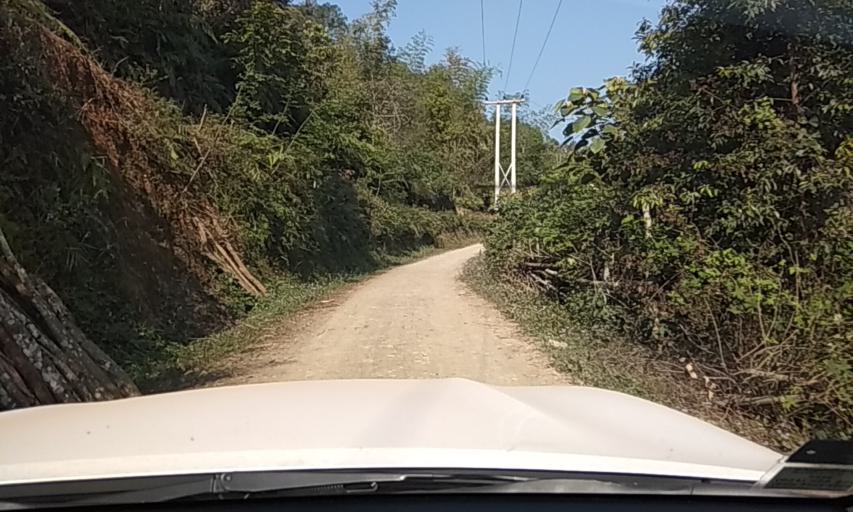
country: LA
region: Phongsali
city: Phongsali
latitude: 21.6969
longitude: 102.0829
